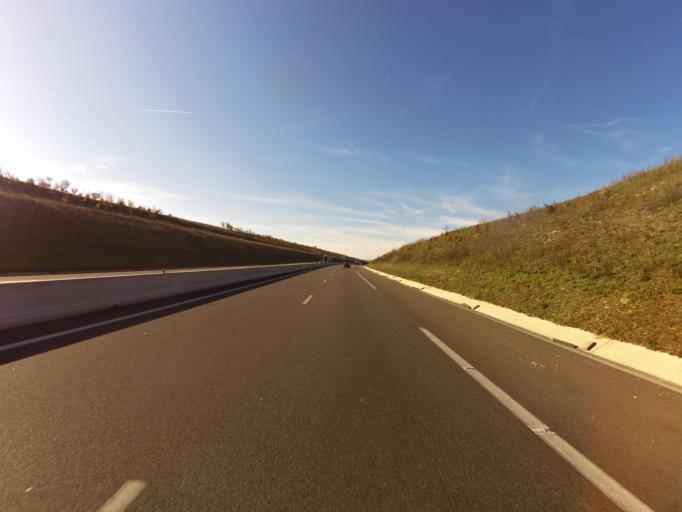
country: FR
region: Champagne-Ardenne
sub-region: Departement de la Marne
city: Cormontreuil
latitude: 49.2072
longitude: 4.0343
